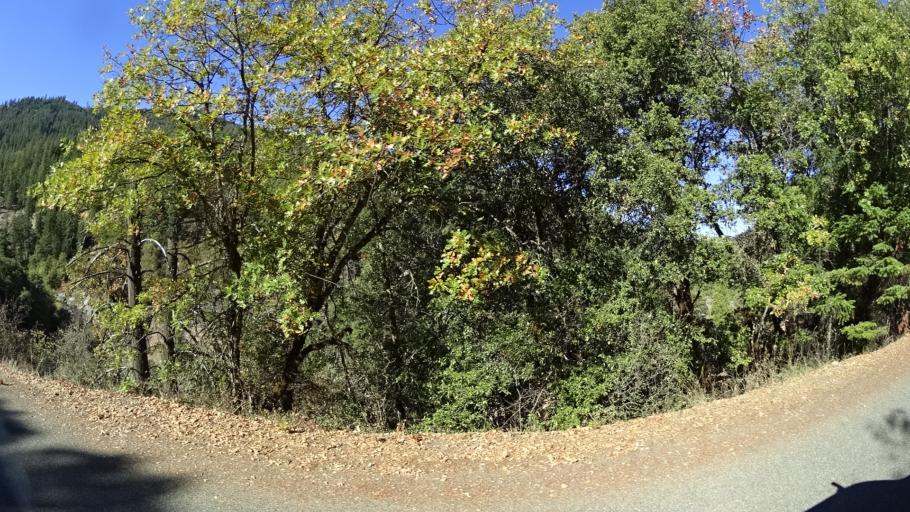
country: US
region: California
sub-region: Humboldt County
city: Willow Creek
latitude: 41.1950
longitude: -123.2151
